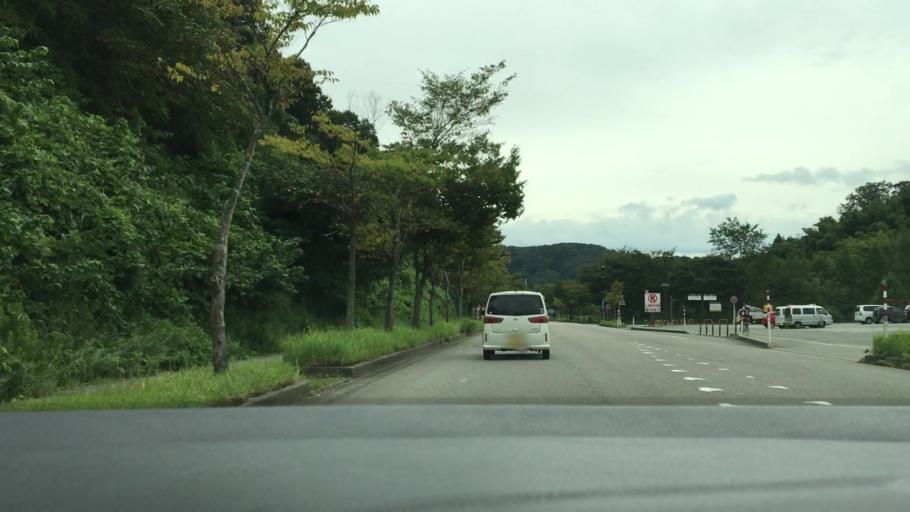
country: JP
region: Ishikawa
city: Kanazawa-shi
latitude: 36.5524
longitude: 136.7026
